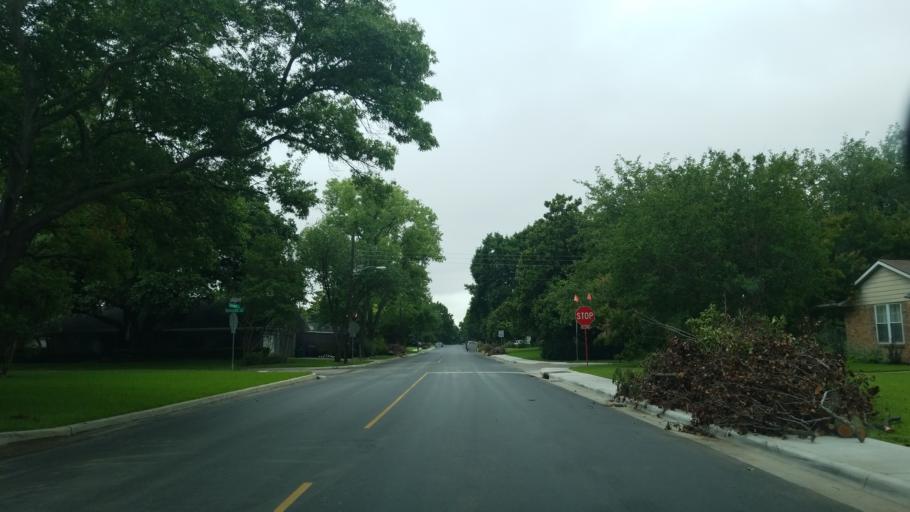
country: US
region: Texas
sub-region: Dallas County
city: Farmers Branch
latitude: 32.8928
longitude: -96.8624
